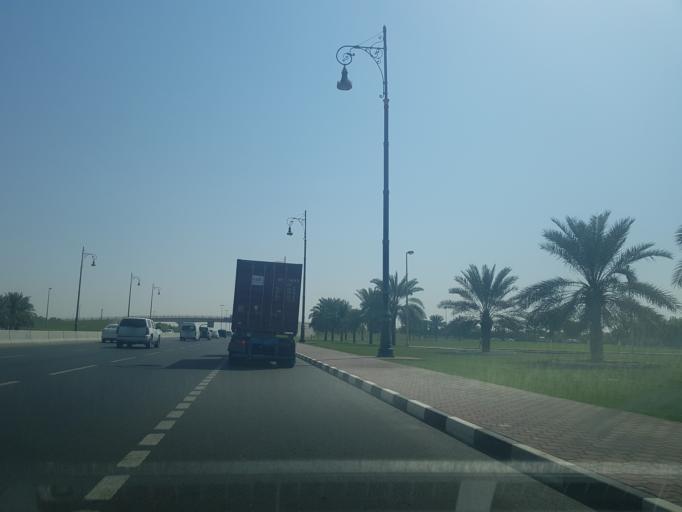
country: AE
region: Ash Shariqah
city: Sharjah
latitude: 25.3139
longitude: 55.5420
